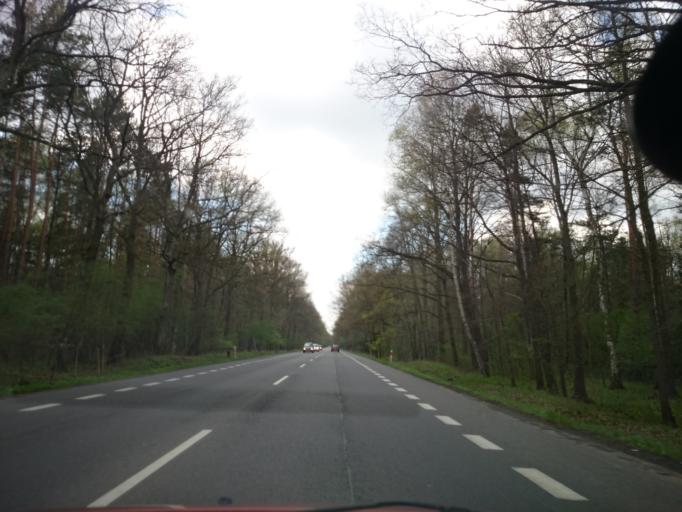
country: PL
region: Opole Voivodeship
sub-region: Powiat opolski
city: Chrzastowice
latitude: 50.6322
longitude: 18.0214
